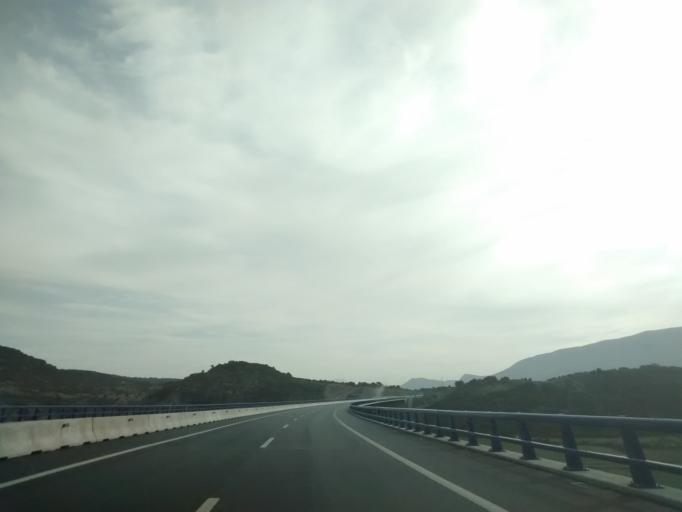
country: ES
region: Aragon
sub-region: Provincia de Zaragoza
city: Siguees
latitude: 42.6251
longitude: -1.0142
